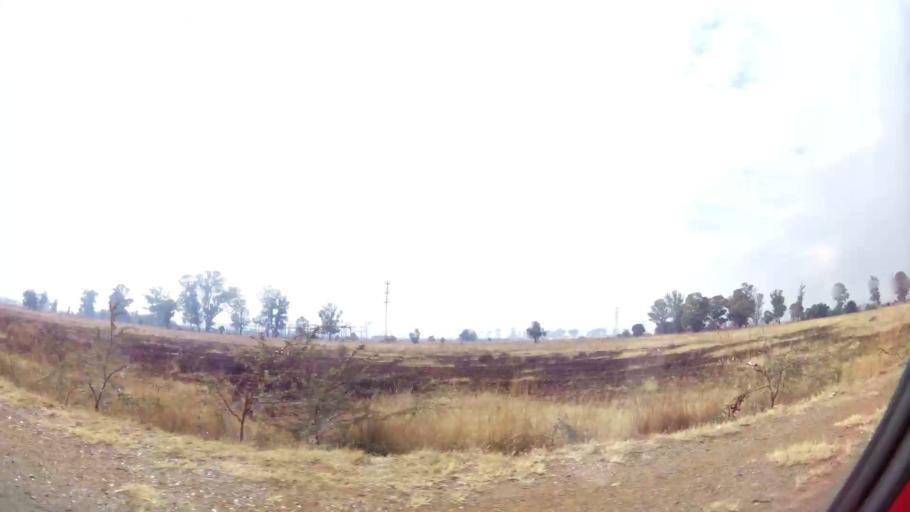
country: ZA
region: Gauteng
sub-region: Sedibeng District Municipality
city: Vanderbijlpark
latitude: -26.6829
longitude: 27.8537
